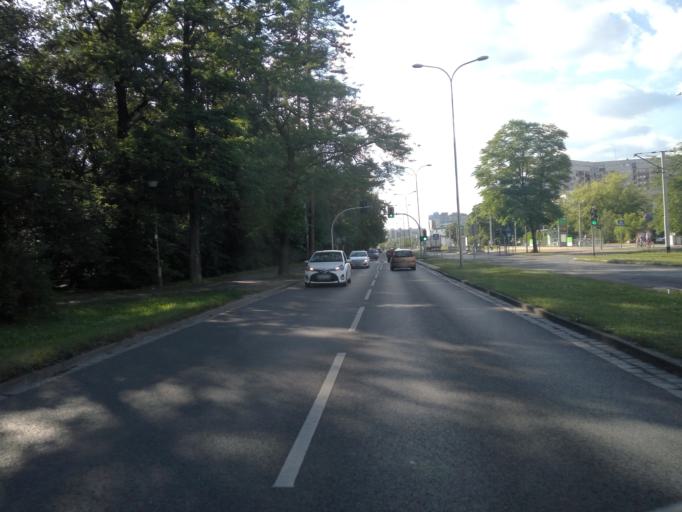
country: PL
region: Lower Silesian Voivodeship
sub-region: Powiat wroclawski
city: Wroclaw
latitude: 51.1345
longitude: 16.9699
